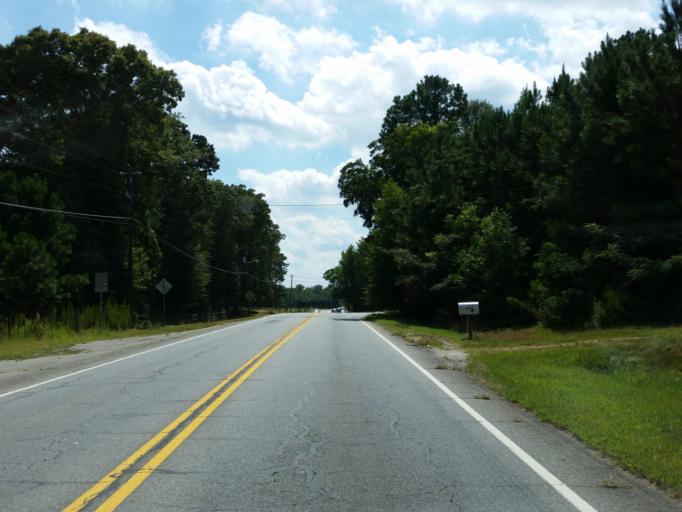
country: US
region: Georgia
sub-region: Gwinnett County
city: Lawrenceville
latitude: 33.9714
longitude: -83.9502
